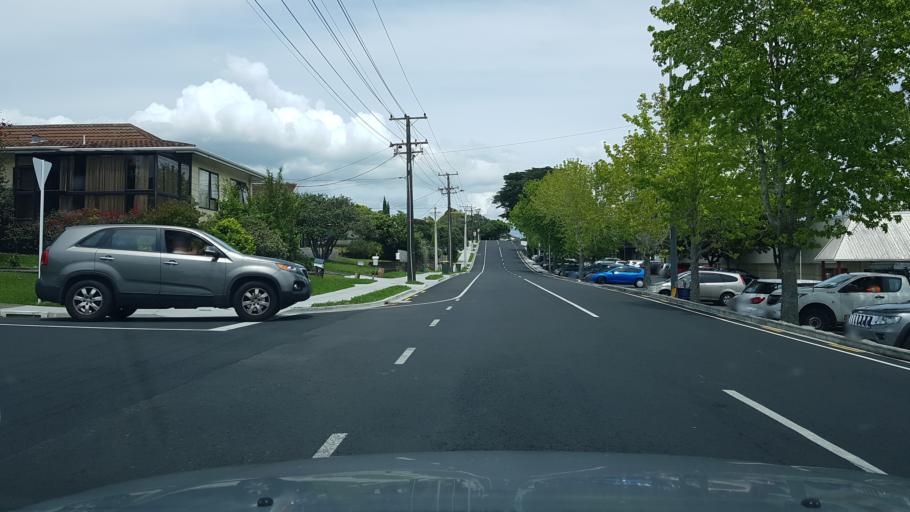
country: NZ
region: Auckland
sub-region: Auckland
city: North Shore
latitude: -36.8015
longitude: 174.7475
